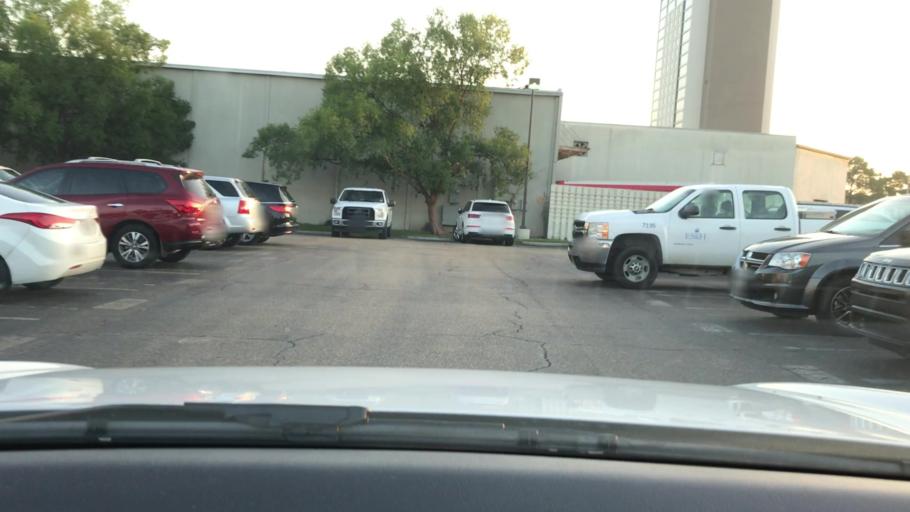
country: US
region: Louisiana
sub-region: East Baton Rouge Parish
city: Baton Rouge
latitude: 30.4212
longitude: -91.1353
